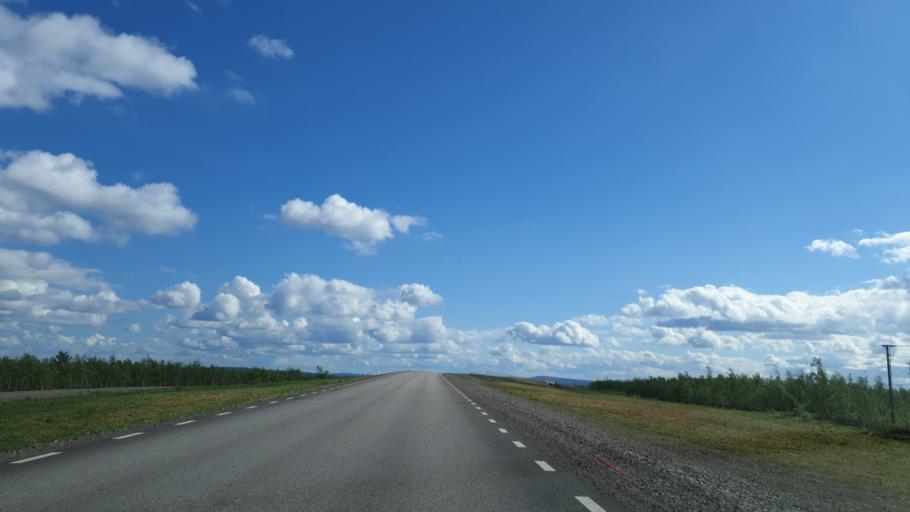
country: SE
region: Norrbotten
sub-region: Kiruna Kommun
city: Kiruna
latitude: 67.7985
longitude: 20.2340
